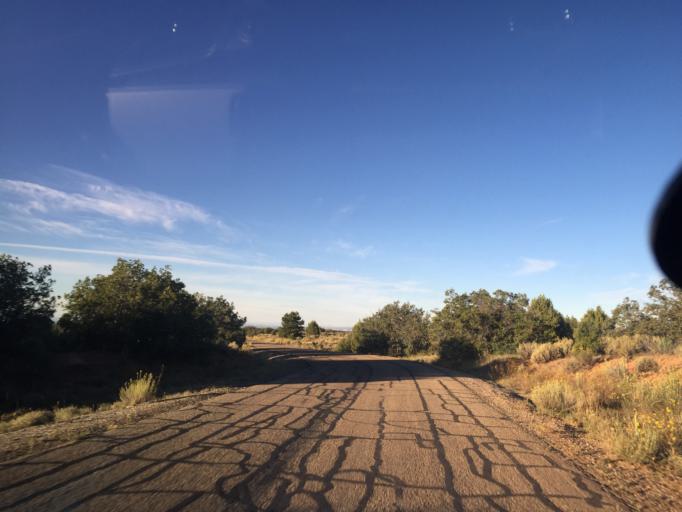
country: US
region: Utah
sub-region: San Juan County
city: Blanding
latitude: 37.7345
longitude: -109.4125
